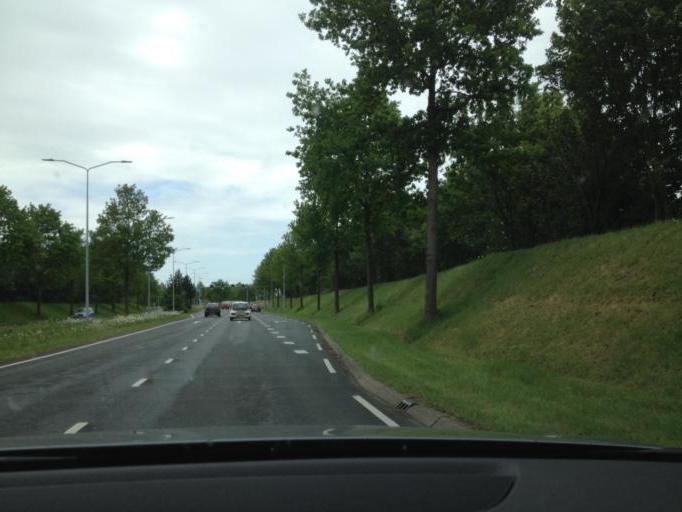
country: NL
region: Flevoland
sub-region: Gemeente Almere
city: Almere Stad
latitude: 52.3645
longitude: 5.2494
